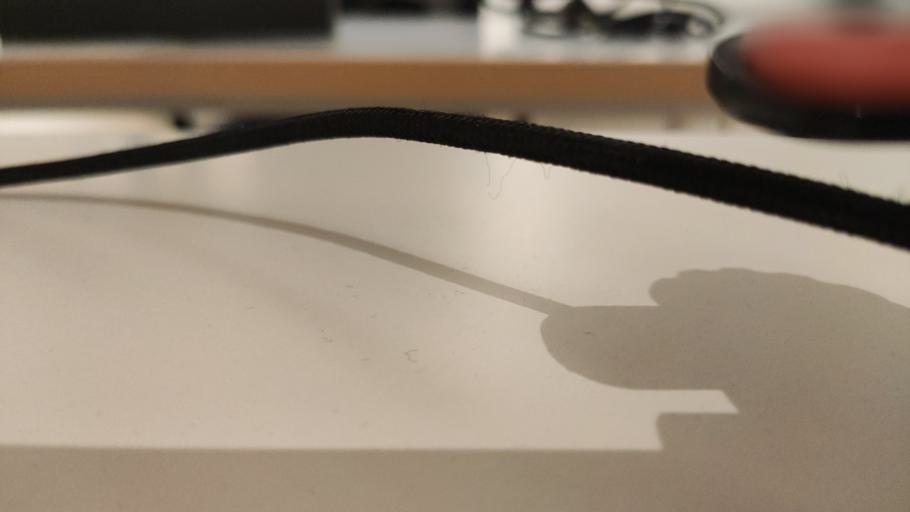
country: RU
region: Moskovskaya
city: Dorokhovo
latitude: 55.4013
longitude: 36.3810
